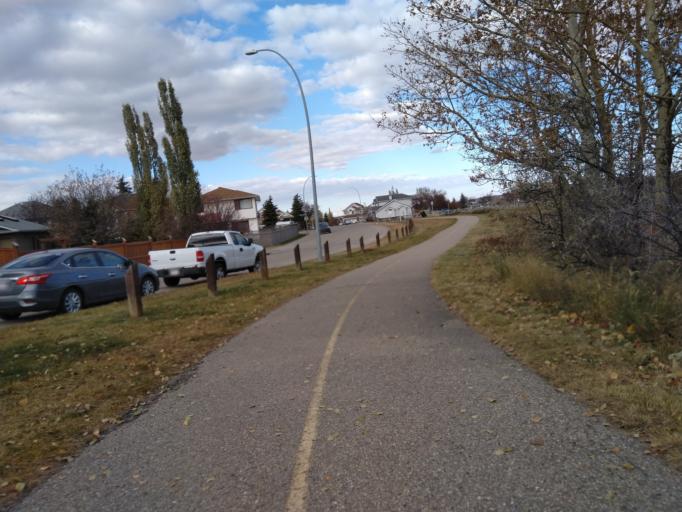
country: CA
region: Alberta
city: Calgary
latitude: 51.1458
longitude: -114.1155
